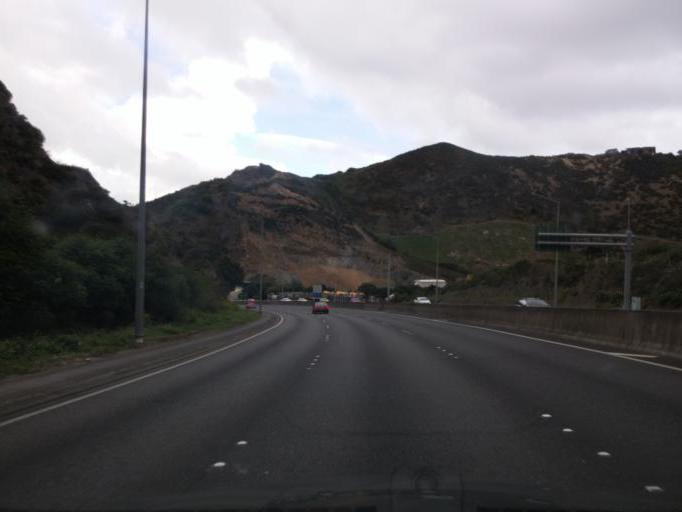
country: NZ
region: Wellington
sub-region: Wellington City
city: Wellington
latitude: -41.2369
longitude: 174.8053
